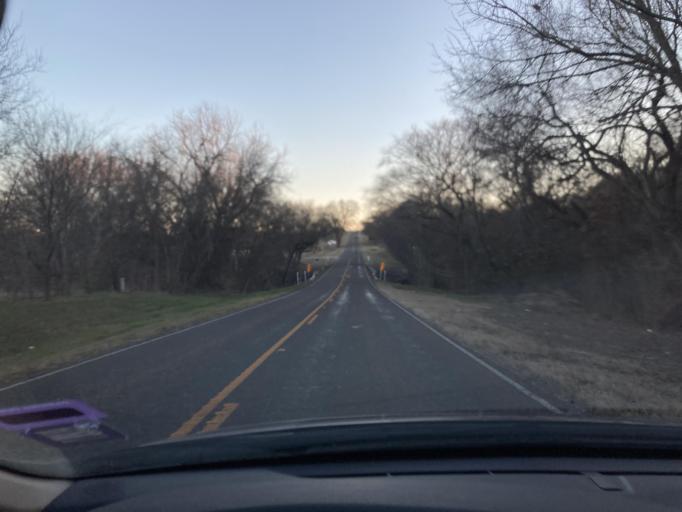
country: US
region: Texas
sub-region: Ellis County
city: Waxahachie
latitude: 32.3507
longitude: -96.8709
